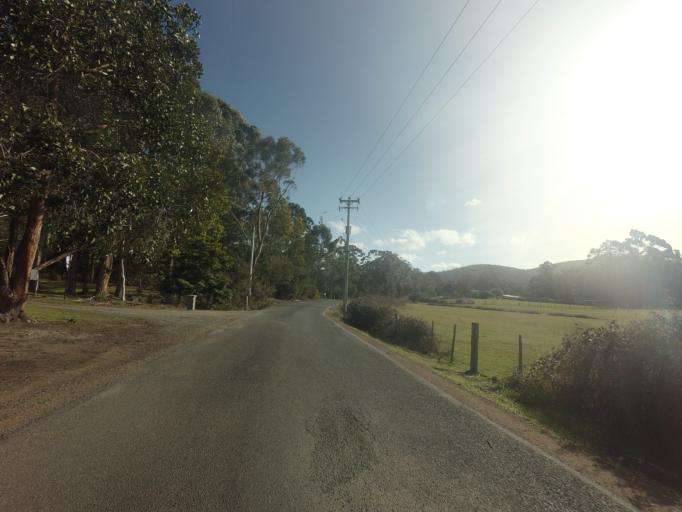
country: AU
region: Tasmania
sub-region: Kingborough
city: Kettering
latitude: -43.1085
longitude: 147.2495
